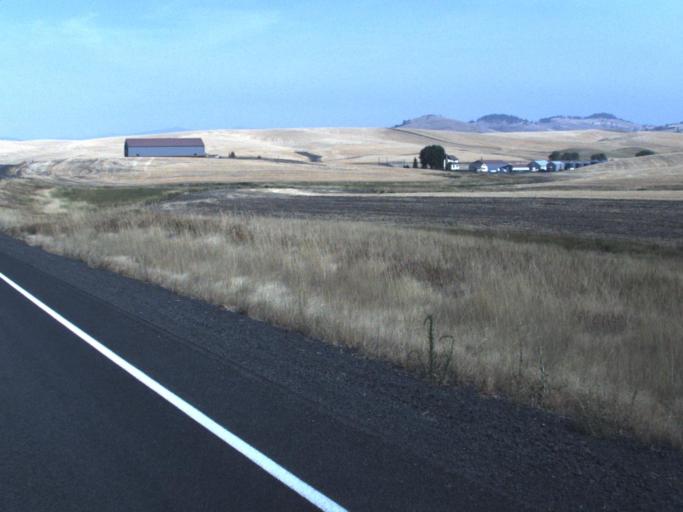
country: US
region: Washington
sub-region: Whitman County
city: Pullman
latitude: 46.8218
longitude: -117.1166
